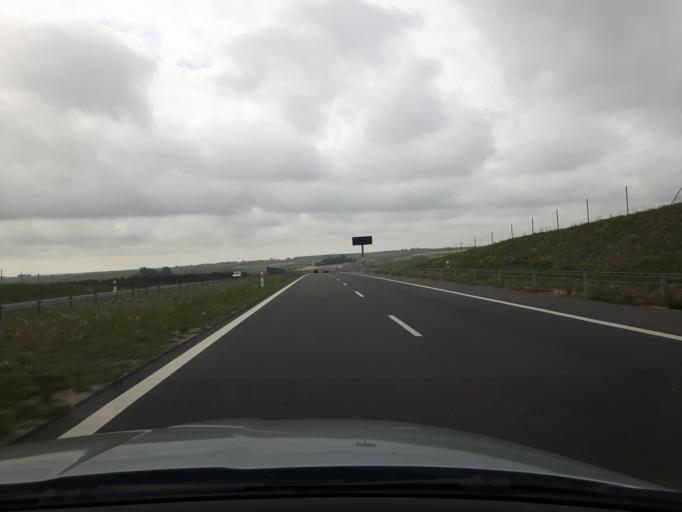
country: PL
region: Swietokrzyskie
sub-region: Powiat jedrzejowski
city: Sobkow
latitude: 50.7149
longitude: 20.4078
